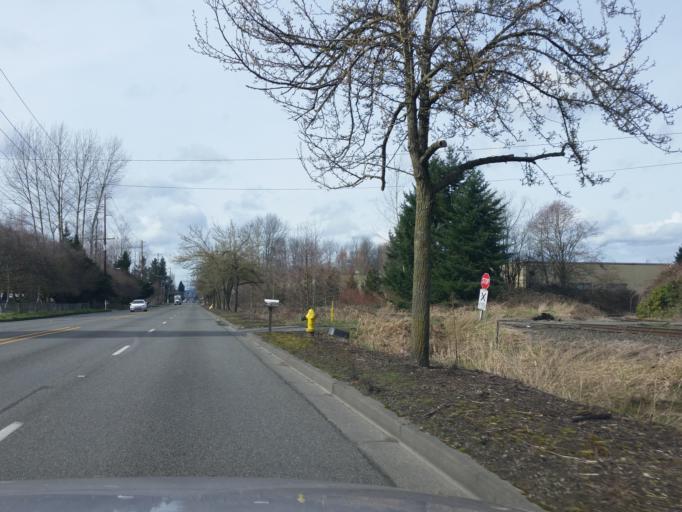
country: US
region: Washington
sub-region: Pierce County
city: Sumner
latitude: 47.1865
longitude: -122.2610
